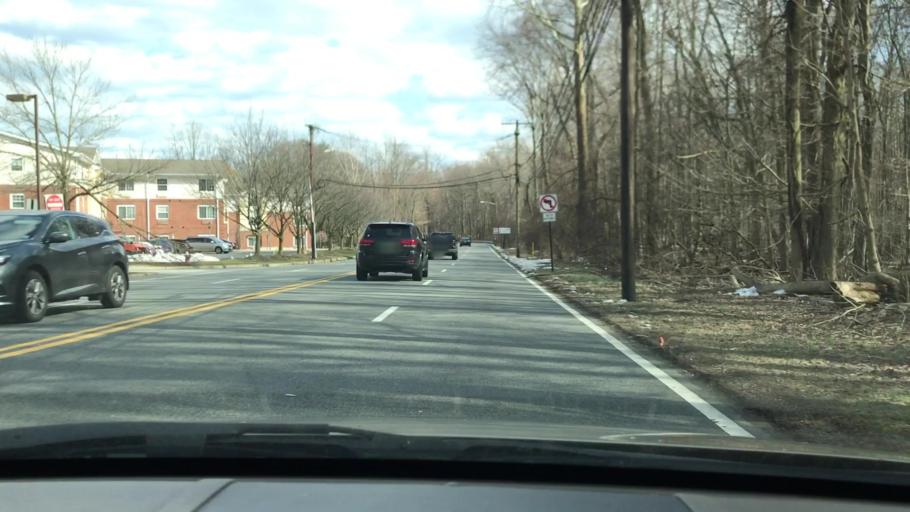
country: US
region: New Jersey
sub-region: Bergen County
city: River Vale
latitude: 40.9797
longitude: -74.0008
